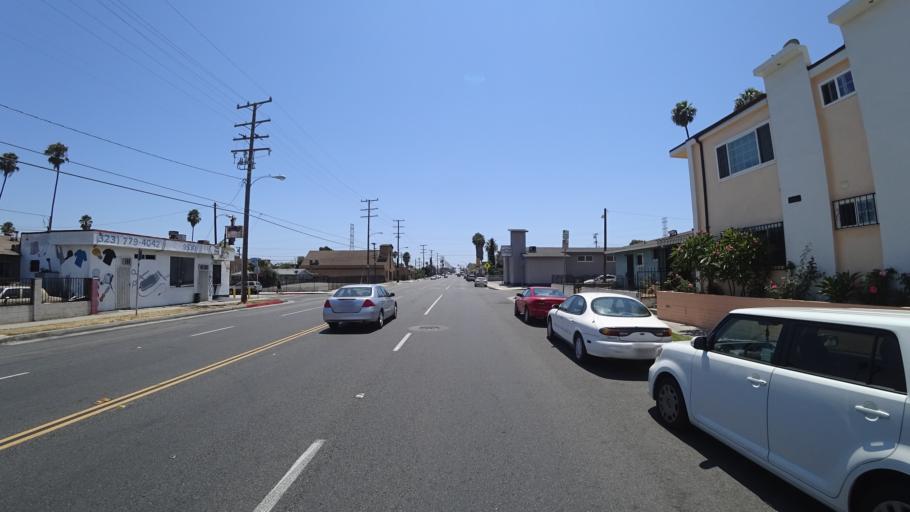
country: US
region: California
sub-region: Los Angeles County
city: Westmont
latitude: 33.9490
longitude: -118.3003
